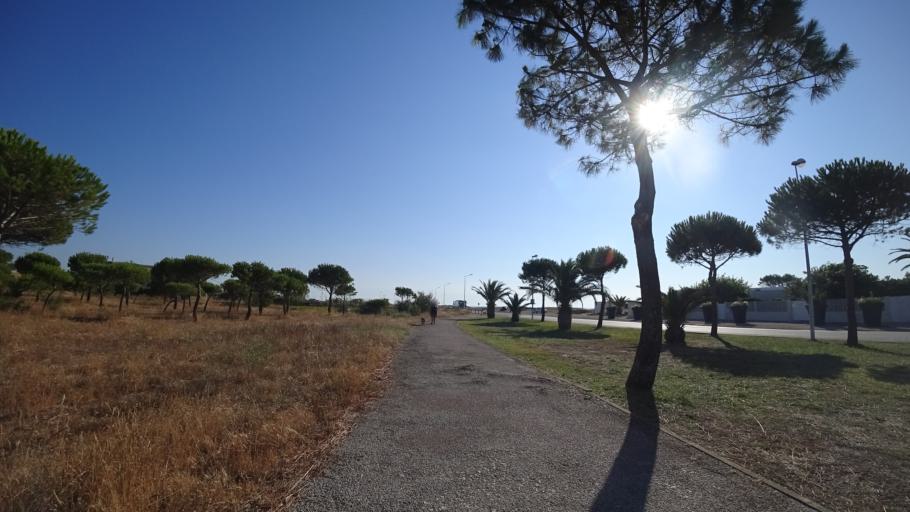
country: FR
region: Languedoc-Roussillon
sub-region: Departement des Pyrenees-Orientales
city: Le Barcares
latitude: 42.8391
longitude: 3.0403
